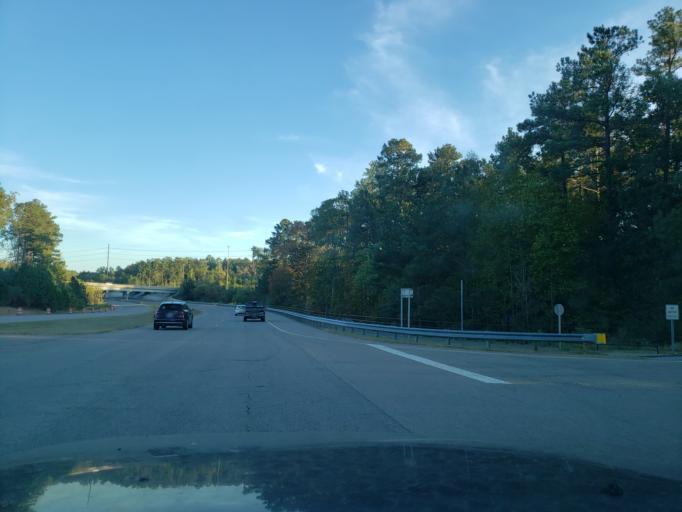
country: US
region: North Carolina
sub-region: Wake County
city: Morrisville
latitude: 35.8540
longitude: -78.8658
